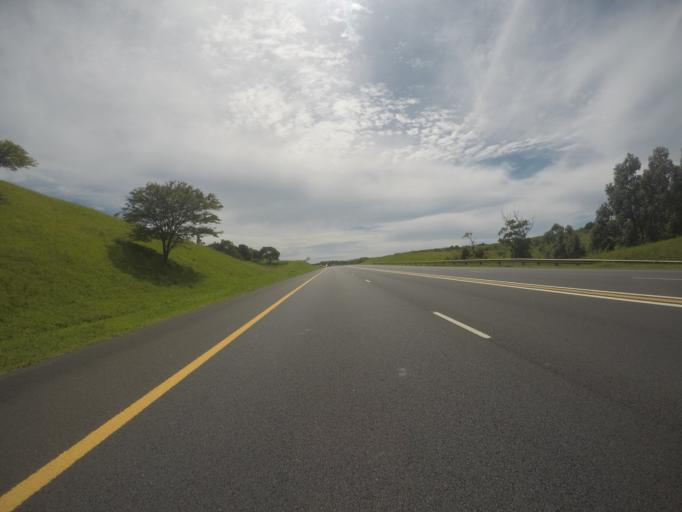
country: ZA
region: KwaZulu-Natal
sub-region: iLembe District Municipality
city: Mandeni
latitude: -29.1664
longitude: 31.5267
